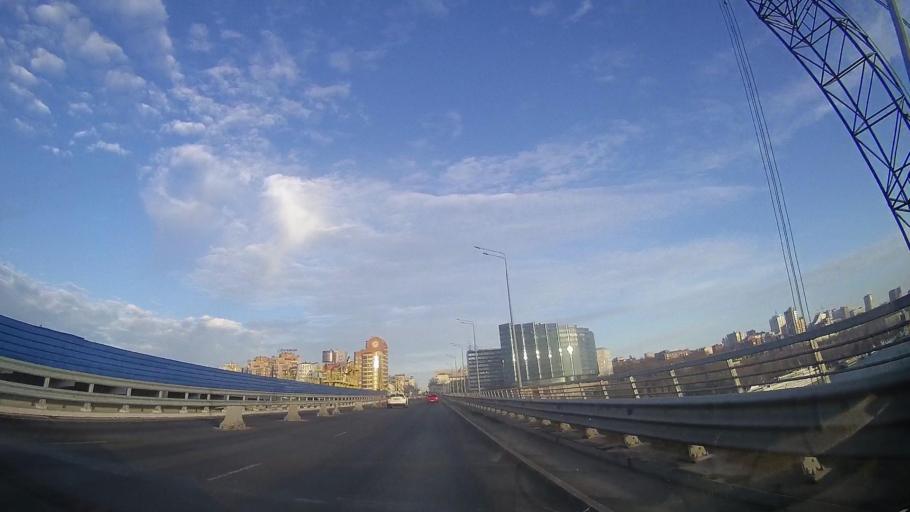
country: RU
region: Rostov
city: Rostov-na-Donu
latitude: 47.2132
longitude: 39.7246
